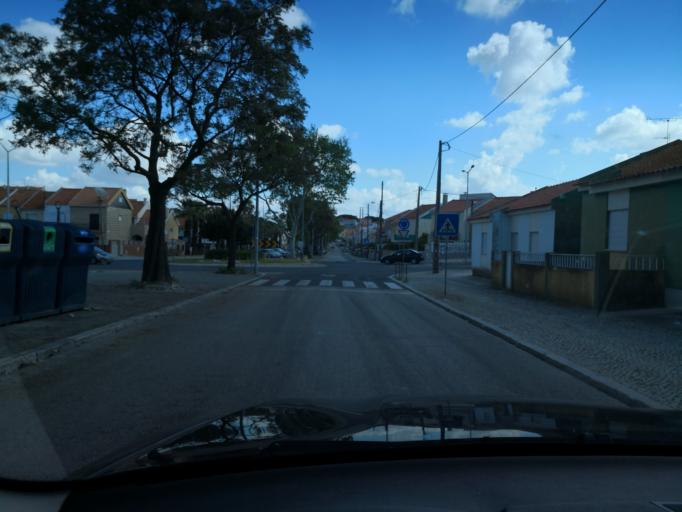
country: PT
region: Setubal
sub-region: Setubal
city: Setubal
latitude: 38.5234
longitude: -8.8637
